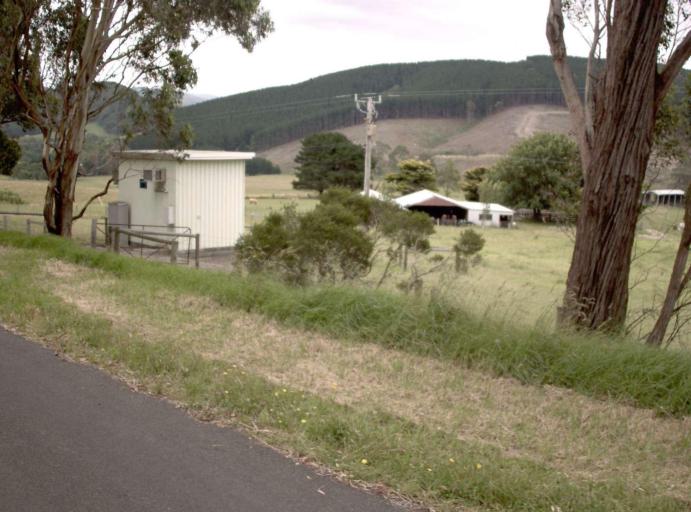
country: AU
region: Victoria
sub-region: Latrobe
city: Traralgon
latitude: -38.4851
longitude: 146.6211
